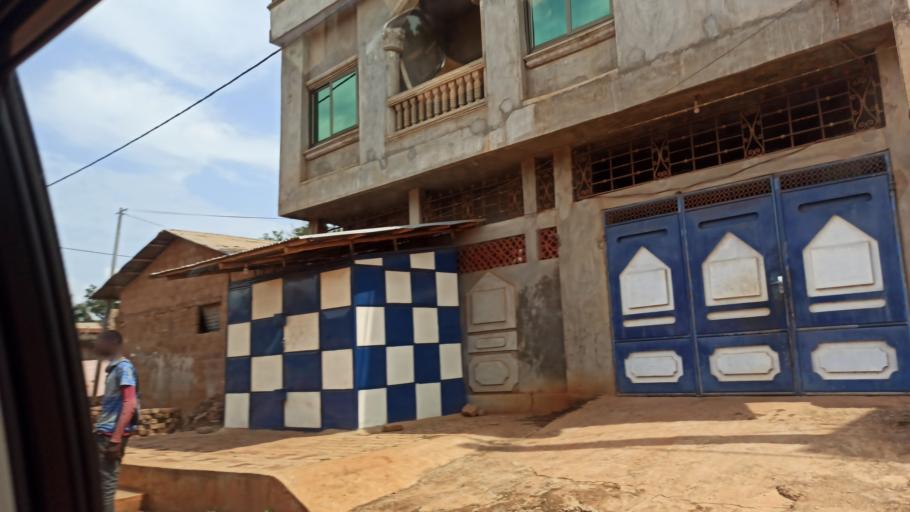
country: BJ
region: Queme
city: Porto-Novo
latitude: 6.4835
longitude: 2.5915
